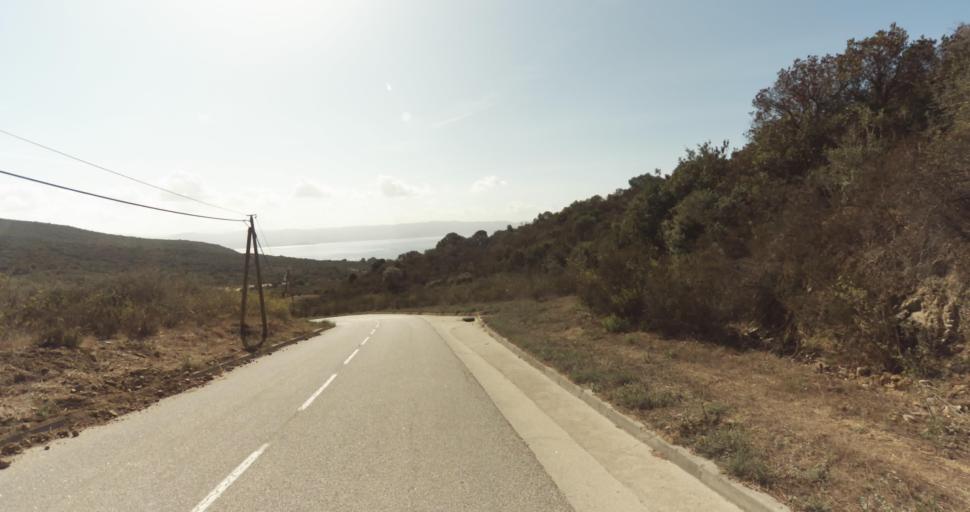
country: FR
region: Corsica
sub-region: Departement de la Corse-du-Sud
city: Ajaccio
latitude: 41.9163
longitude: 8.6427
